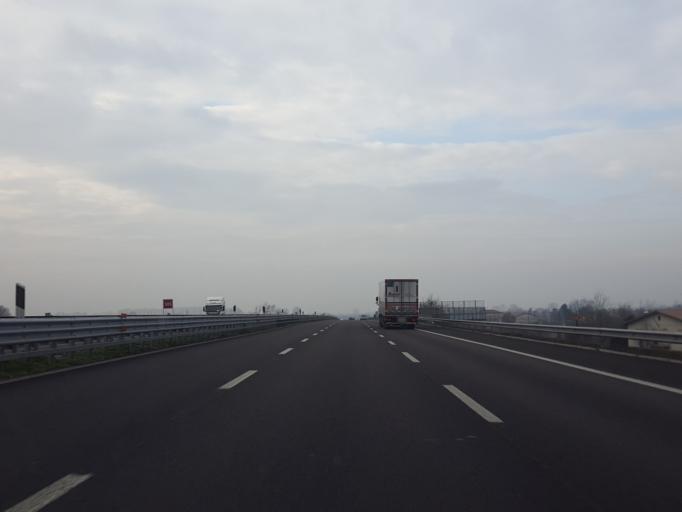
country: IT
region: Veneto
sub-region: Provincia di Padova
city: Ronchi di Campanile
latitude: 45.4658
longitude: 11.7560
